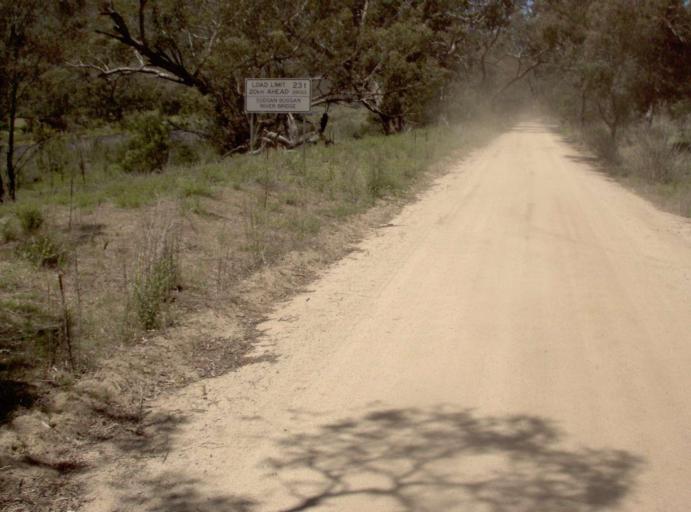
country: AU
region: New South Wales
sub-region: Snowy River
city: Jindabyne
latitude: -36.8863
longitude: 148.4193
